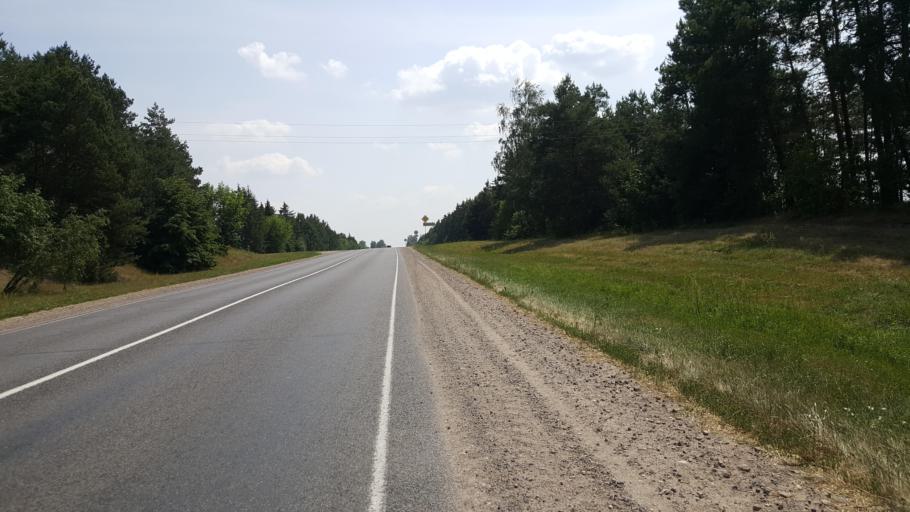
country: BY
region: Brest
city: Kamyanyets
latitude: 52.3383
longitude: 23.7810
